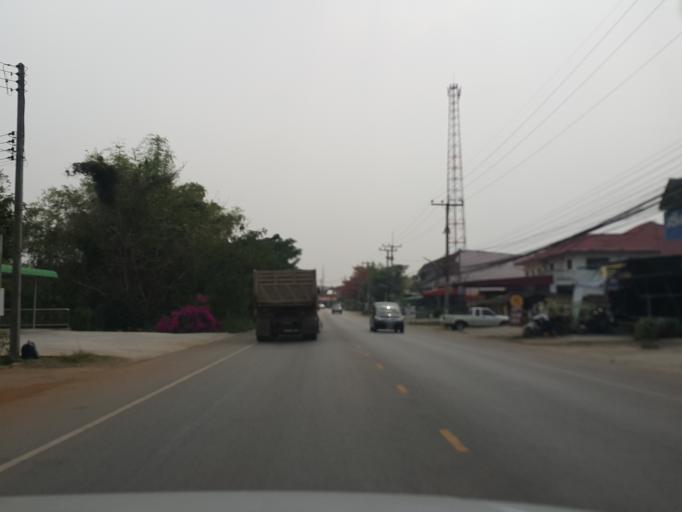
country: TH
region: Lampang
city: Ko Kha
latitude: 18.1980
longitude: 99.3914
